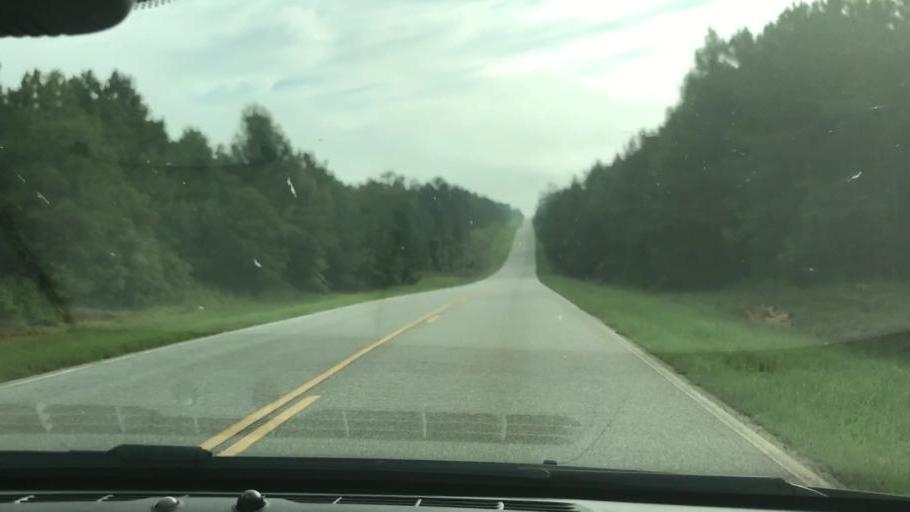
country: US
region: Georgia
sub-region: Stewart County
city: Lumpkin
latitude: 32.0185
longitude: -84.9272
